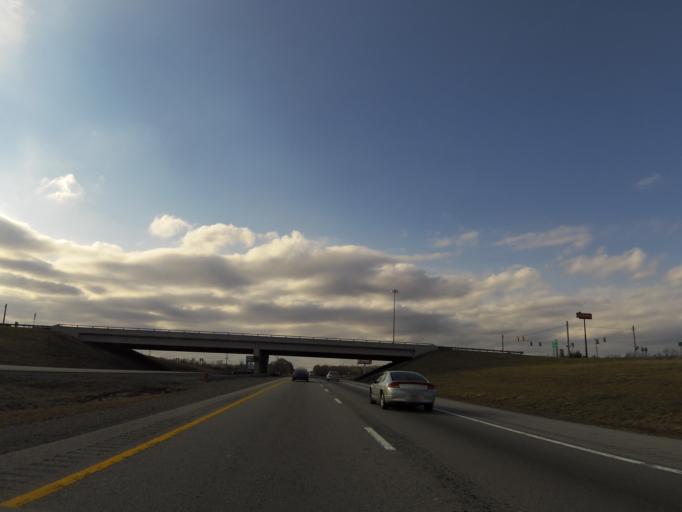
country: US
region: Tennessee
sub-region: Cumberland County
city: Crossville
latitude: 35.9628
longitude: -84.9815
